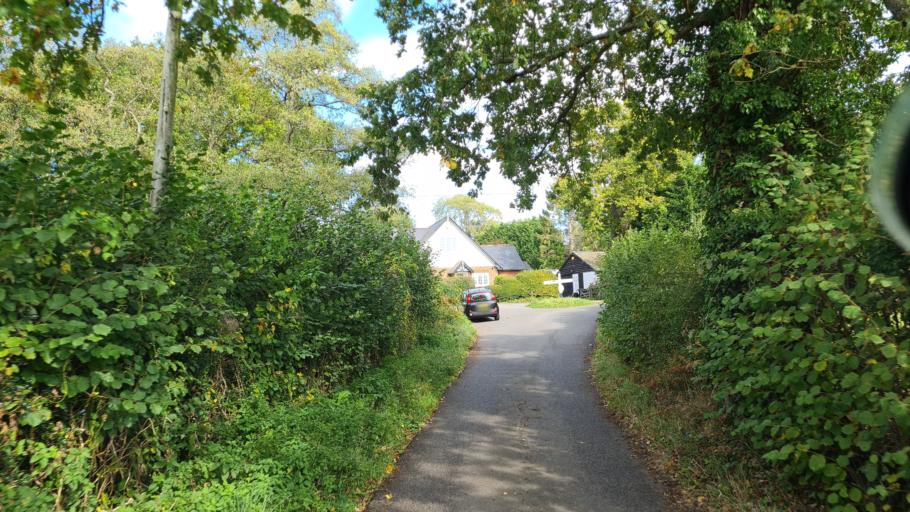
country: GB
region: England
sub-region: East Sussex
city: Battle
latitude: 50.9238
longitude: 0.5462
